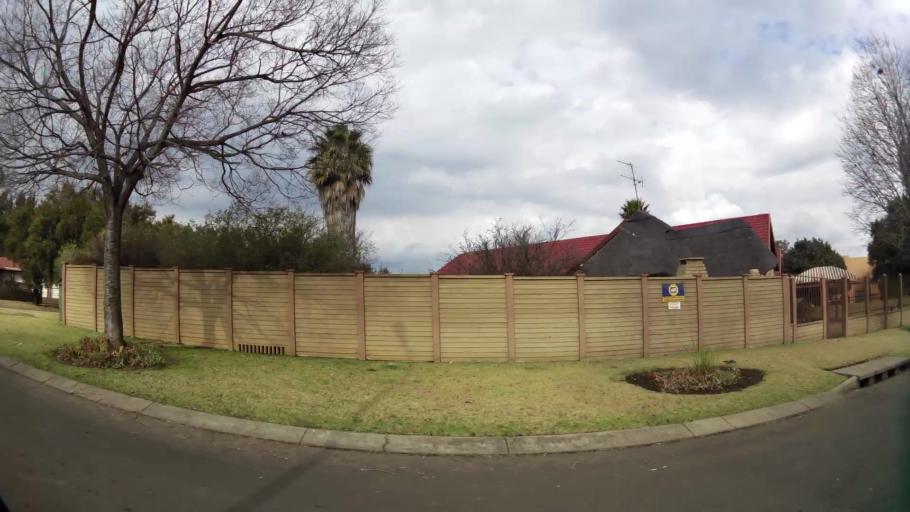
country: ZA
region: Gauteng
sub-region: Sedibeng District Municipality
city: Vanderbijlpark
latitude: -26.7056
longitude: 27.8027
